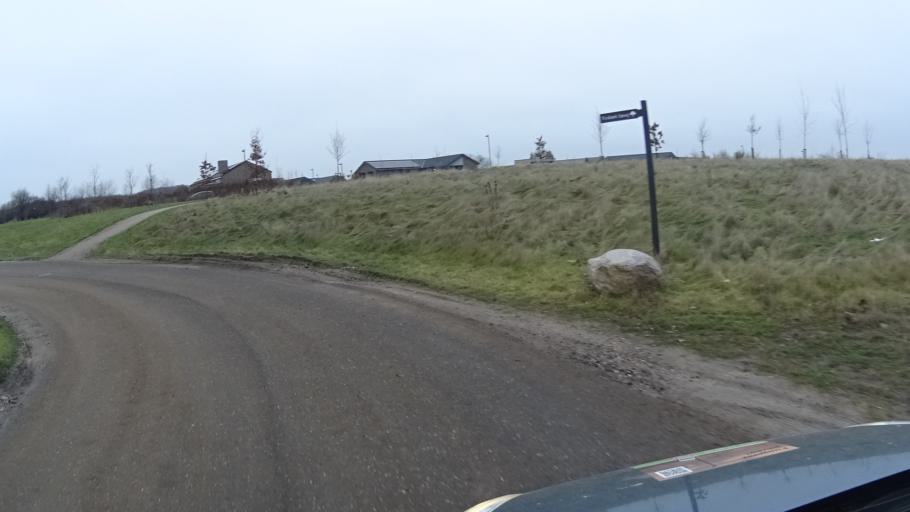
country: DK
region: South Denmark
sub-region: Vejle Kommune
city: Vejle
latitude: 55.7289
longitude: 9.6175
